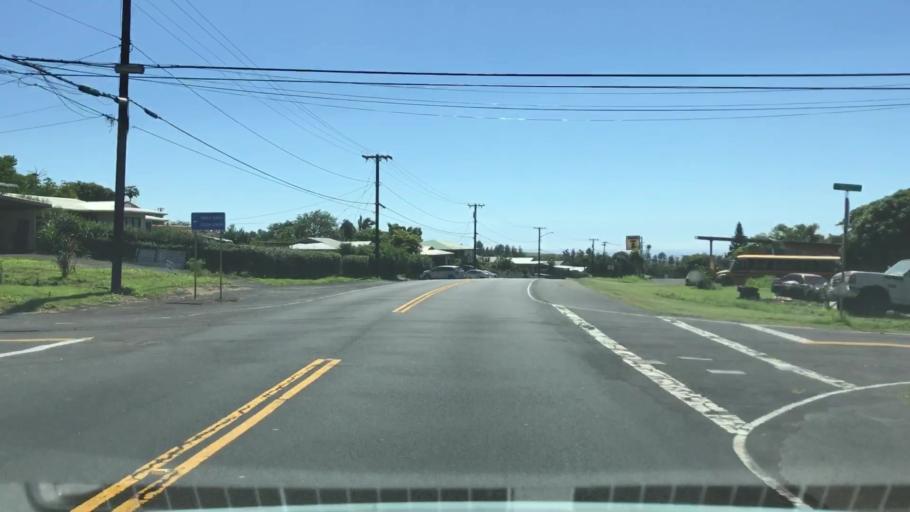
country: US
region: Hawaii
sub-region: Hawaii County
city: Pahala
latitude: 19.2024
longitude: -155.4755
